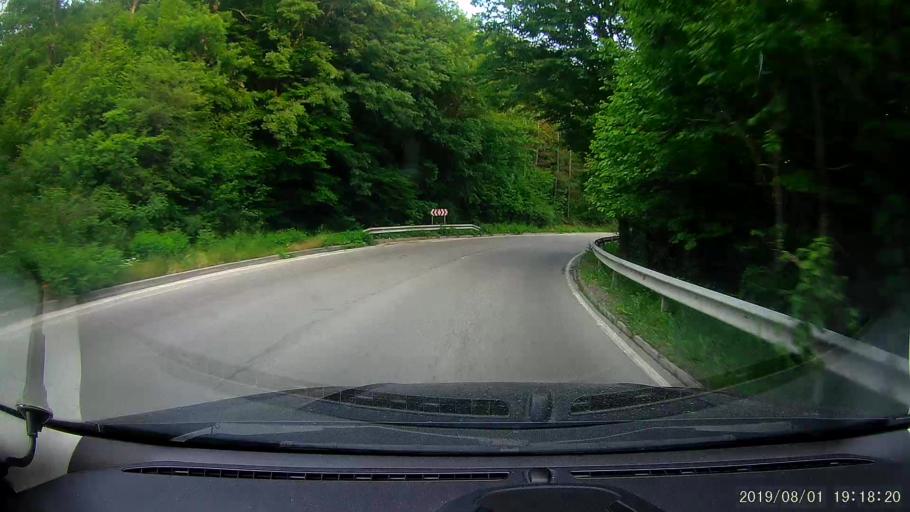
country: BG
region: Shumen
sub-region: Obshtina Smyadovo
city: Smyadovo
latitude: 42.9144
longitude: 26.9403
